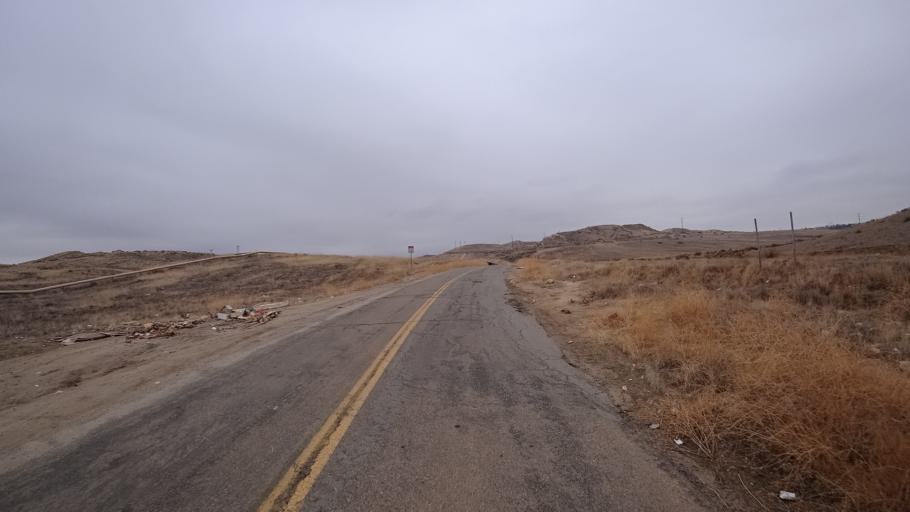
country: US
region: California
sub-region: Kern County
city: Oildale
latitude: 35.4240
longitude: -118.9402
